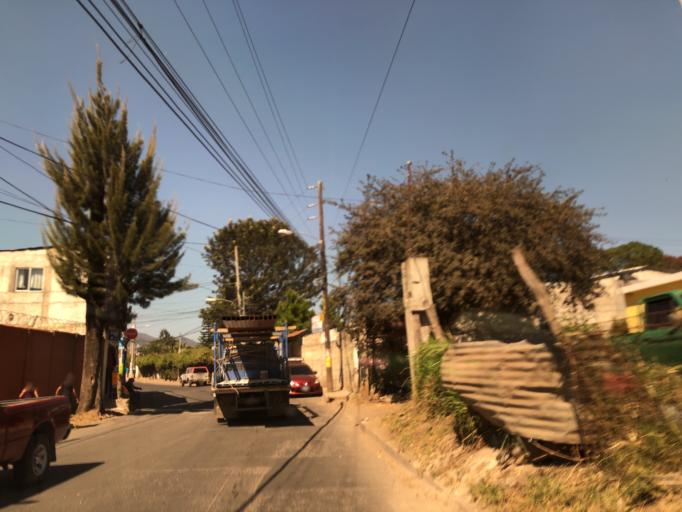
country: GT
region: Guatemala
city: Mixco
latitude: 14.6170
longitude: -90.5796
